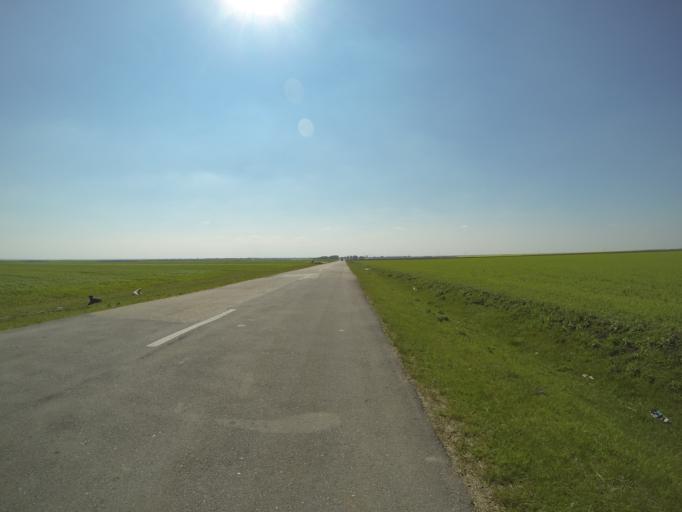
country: RO
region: Dolj
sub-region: Comuna Caraula
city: Caraula
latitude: 44.1791
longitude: 23.2113
